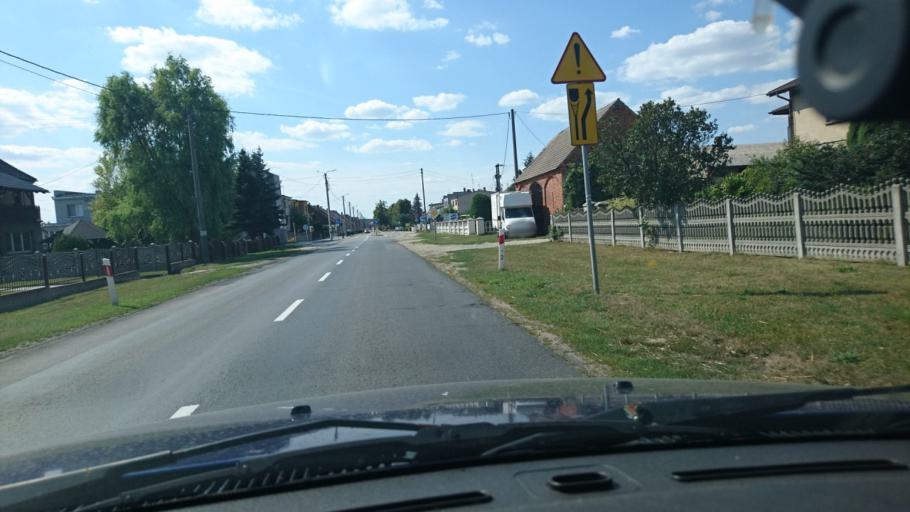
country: PL
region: Greater Poland Voivodeship
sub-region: Powiat krotoszynski
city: Sulmierzyce
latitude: 51.6056
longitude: 17.5406
